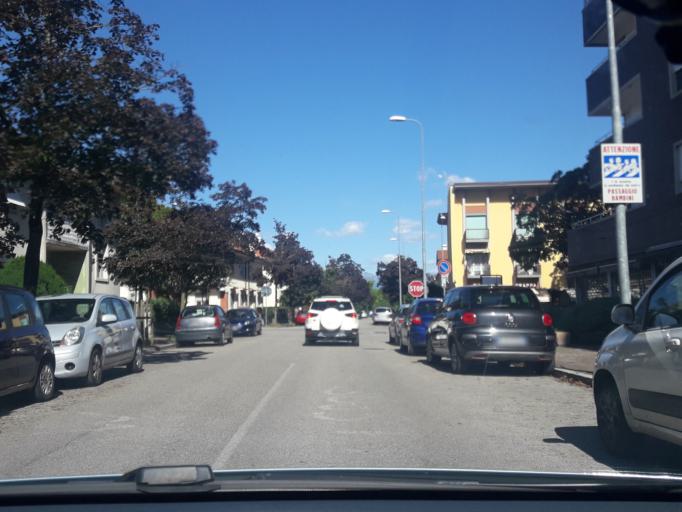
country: IT
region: Friuli Venezia Giulia
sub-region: Provincia di Udine
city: Udine
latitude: 46.0766
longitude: 13.2430
